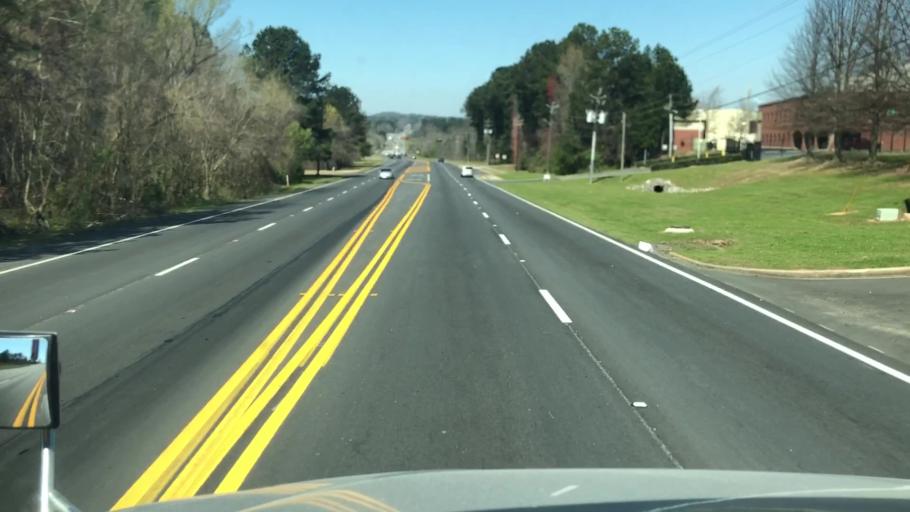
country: US
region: Georgia
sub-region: Cobb County
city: Mableton
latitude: 33.7751
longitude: -84.5267
